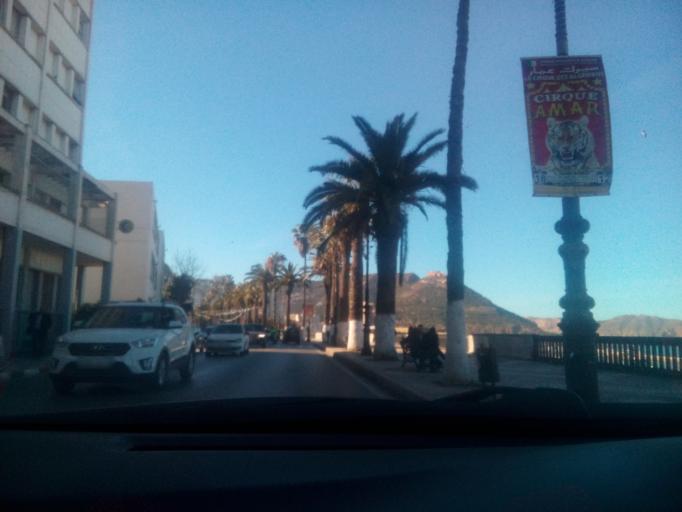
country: DZ
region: Oran
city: Oran
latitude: 35.7068
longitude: -0.6323
